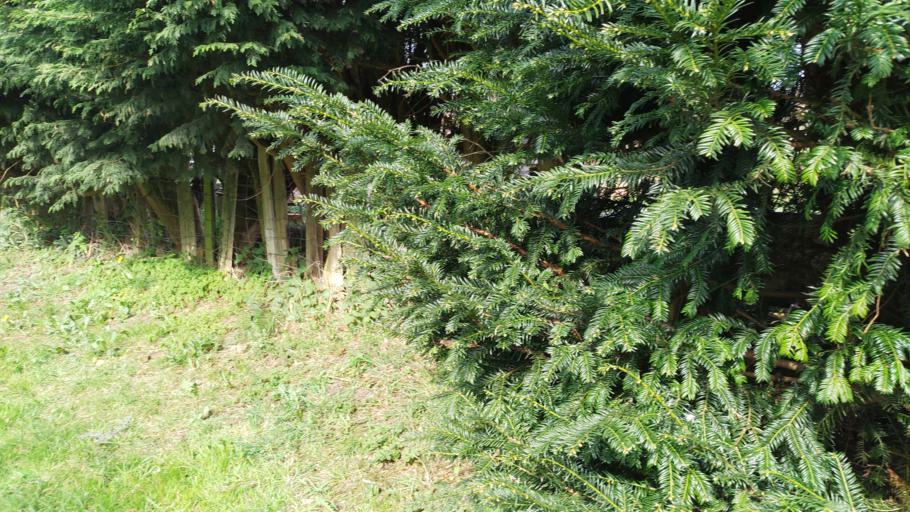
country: GB
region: England
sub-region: Lancashire
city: Chorley
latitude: 53.6714
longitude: -2.5908
